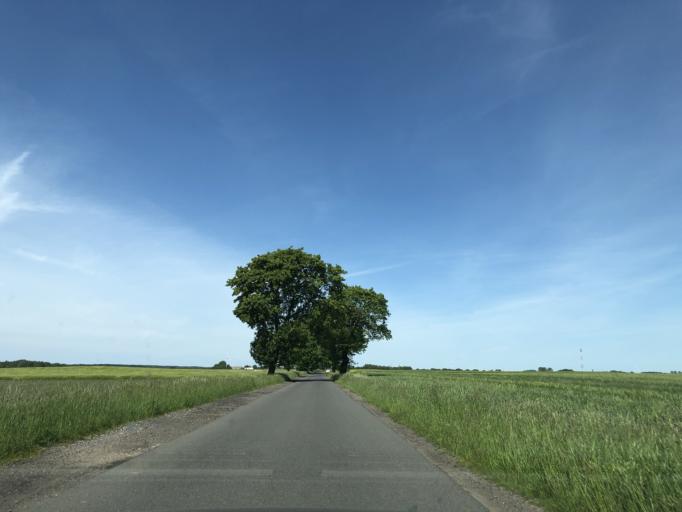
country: PL
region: West Pomeranian Voivodeship
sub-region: Powiat kolobrzeski
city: Dygowo
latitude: 54.1144
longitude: 15.7056
